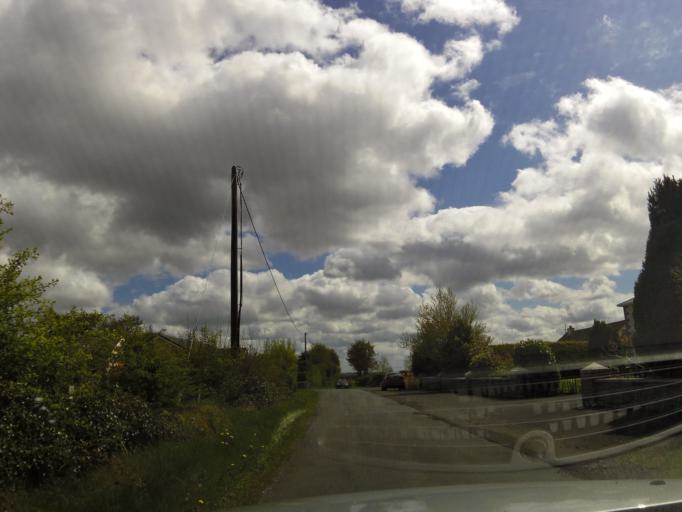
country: IE
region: Connaught
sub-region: Maigh Eo
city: Claremorris
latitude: 53.7774
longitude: -8.9603
